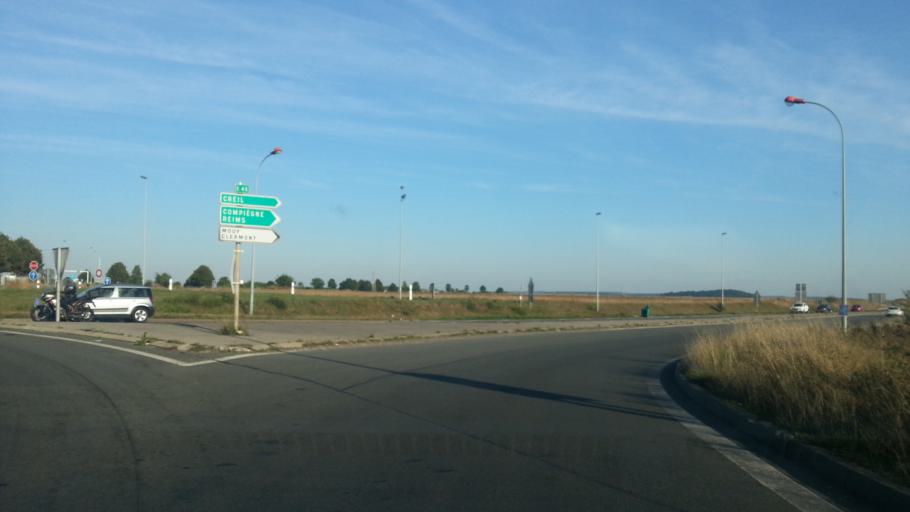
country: FR
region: Picardie
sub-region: Departement de l'Oise
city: Allonne
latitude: 49.4327
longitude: 2.1215
